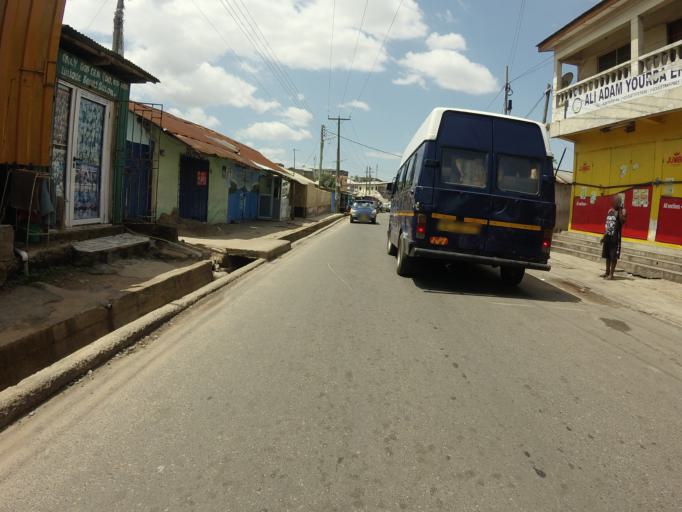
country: GH
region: Greater Accra
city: Accra
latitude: 5.5798
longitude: -0.2030
